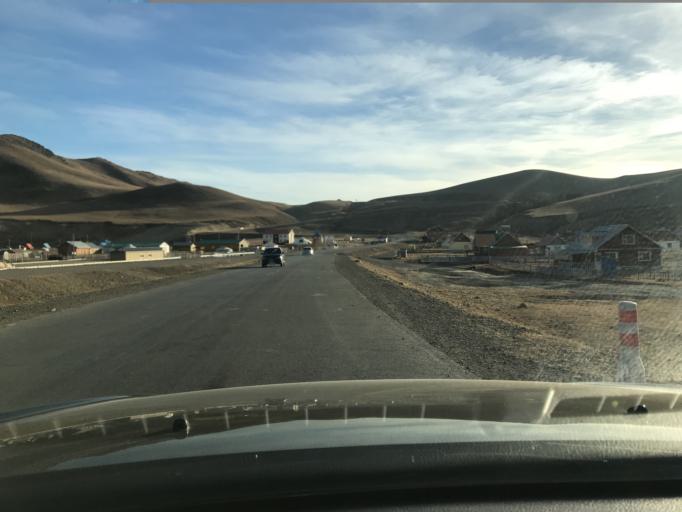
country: MN
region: Central Aimak
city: Dzuunmod
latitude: 47.8196
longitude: 107.3307
